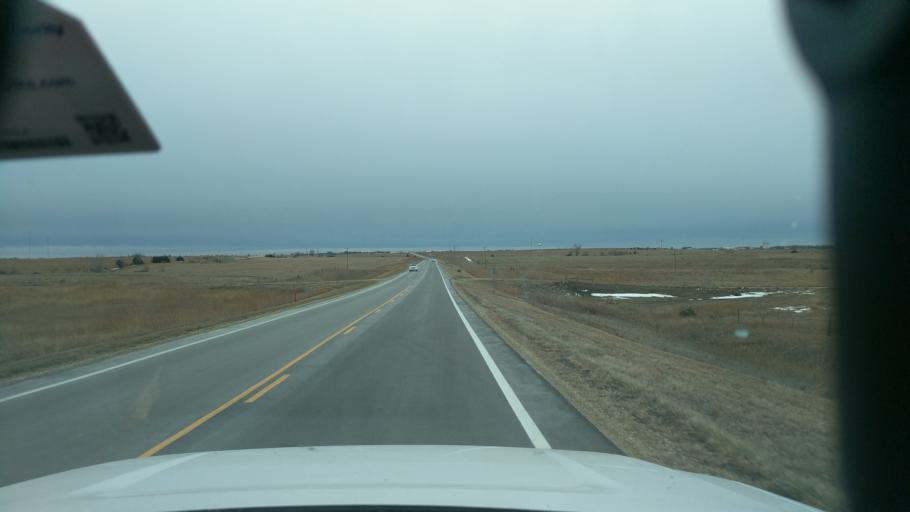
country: US
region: Kansas
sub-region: Dickinson County
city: Herington
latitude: 38.7043
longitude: -96.9293
